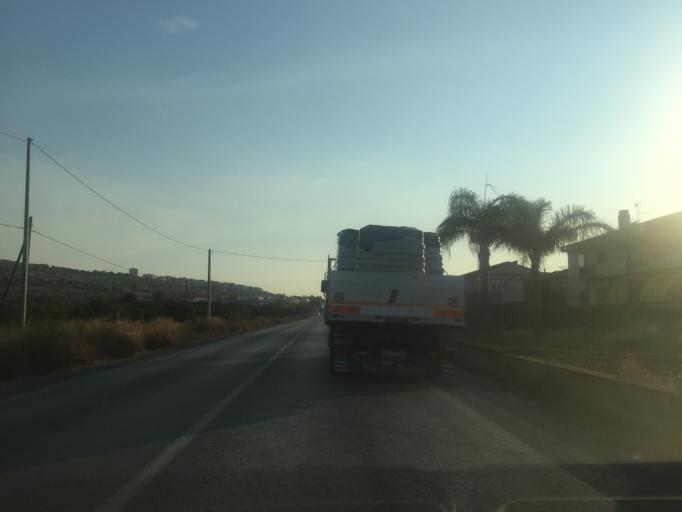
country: IT
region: Sicily
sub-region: Ragusa
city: Ispica
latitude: 36.7662
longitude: 14.9010
